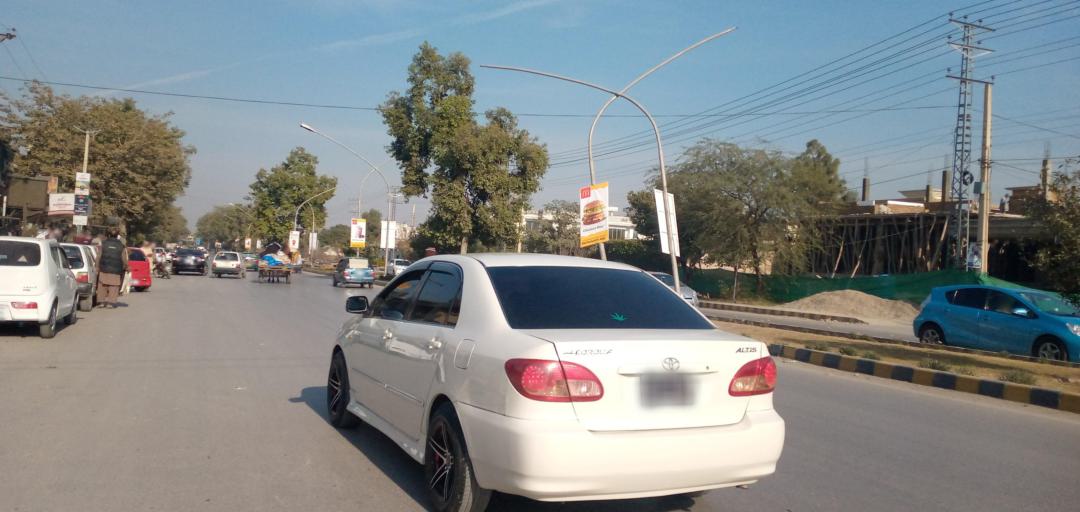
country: PK
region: Khyber Pakhtunkhwa
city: Peshawar
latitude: 33.9736
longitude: 71.4437
